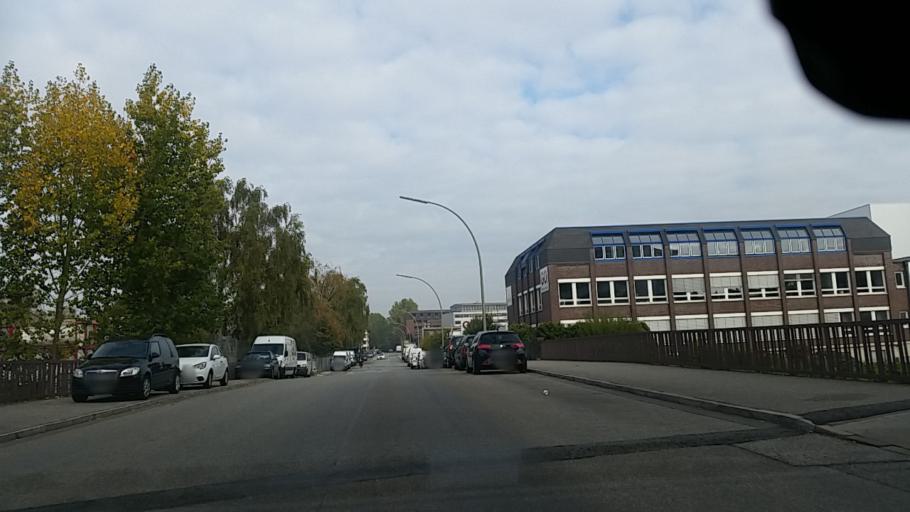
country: DE
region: Hamburg
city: Rothenburgsort
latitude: 53.5483
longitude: 10.0512
